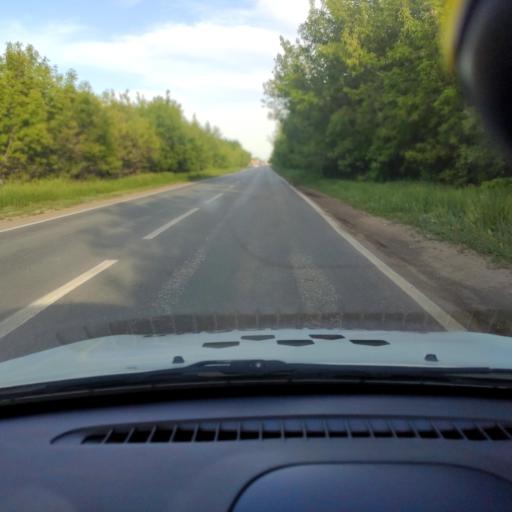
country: RU
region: Samara
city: Podstepki
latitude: 53.5781
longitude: 49.0705
